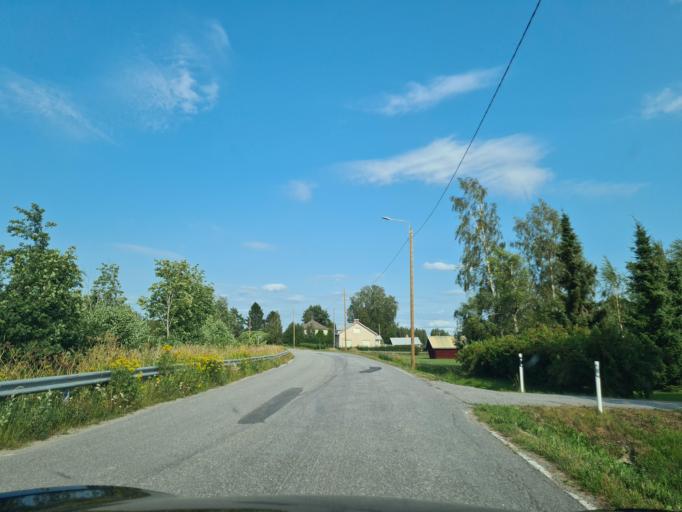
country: FI
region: Ostrobothnia
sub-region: Vaasa
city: Ristinummi
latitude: 63.0319
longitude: 21.8563
